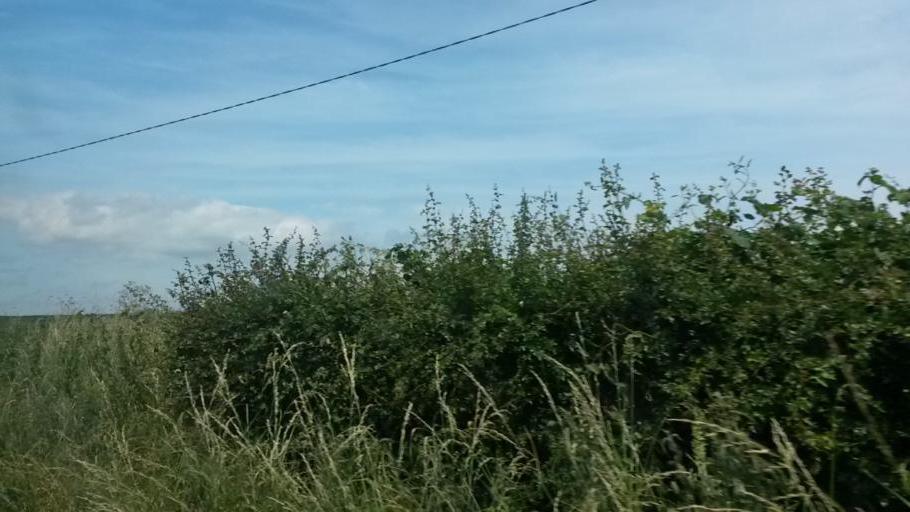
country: IE
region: Leinster
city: Lusk
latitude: 53.5343
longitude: -6.1785
